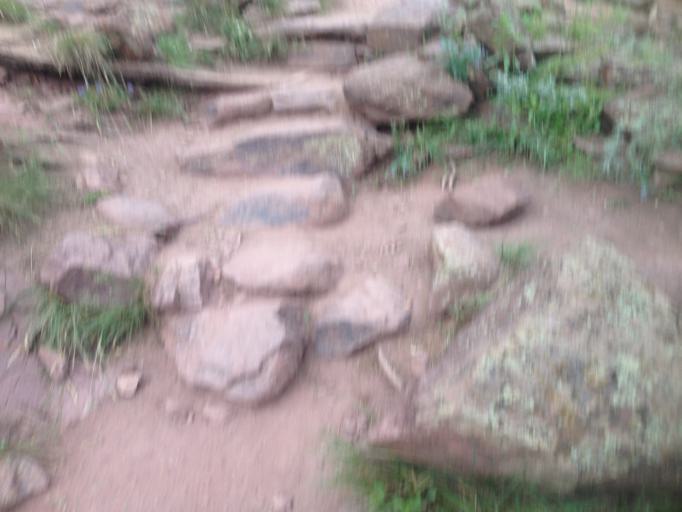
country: US
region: Colorado
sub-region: Boulder County
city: Boulder
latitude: 40.0333
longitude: -105.3053
